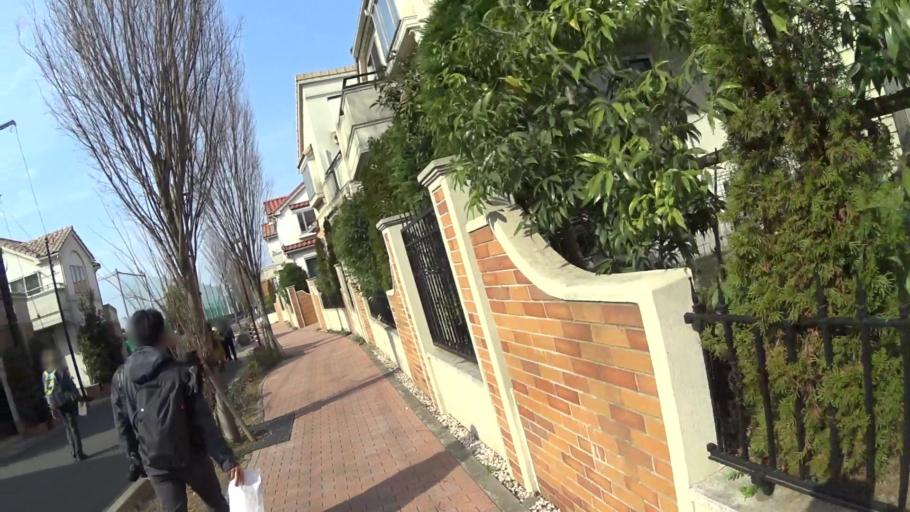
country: JP
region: Chiba
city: Funabashi
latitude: 35.6942
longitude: 140.0055
